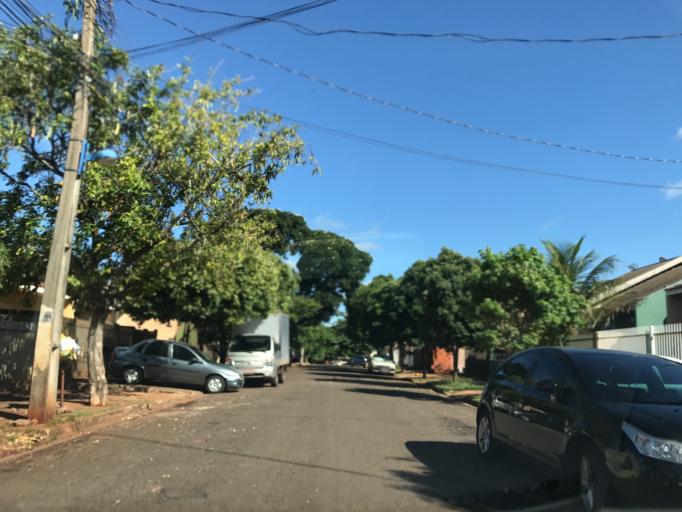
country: BR
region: Parana
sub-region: Maringa
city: Maringa
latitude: -23.4563
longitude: -51.9591
